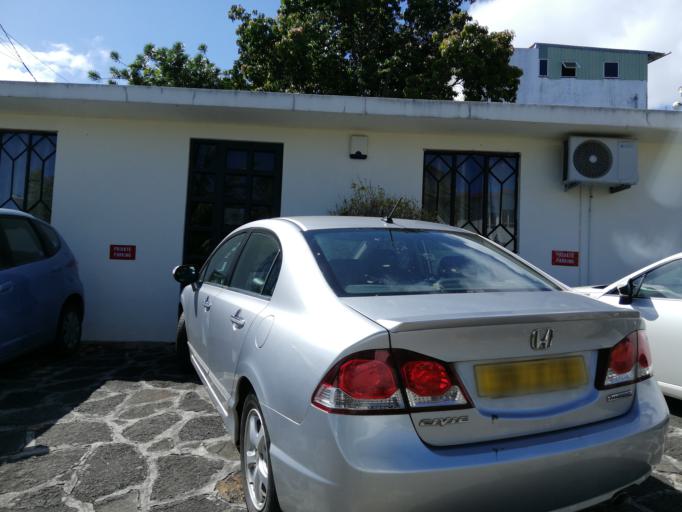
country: MU
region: Moka
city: Moka
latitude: -20.2305
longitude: 57.4980
